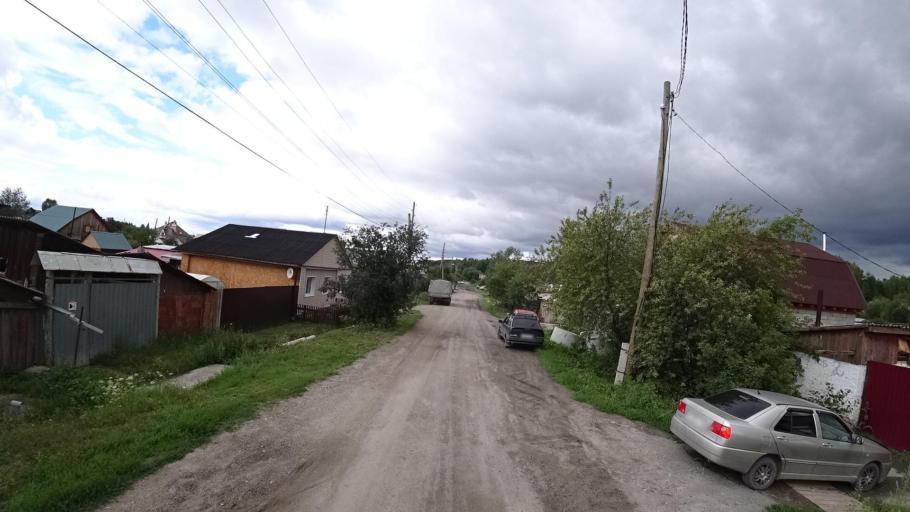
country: RU
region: Sverdlovsk
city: Kamyshlov
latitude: 56.8570
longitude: 62.7185
